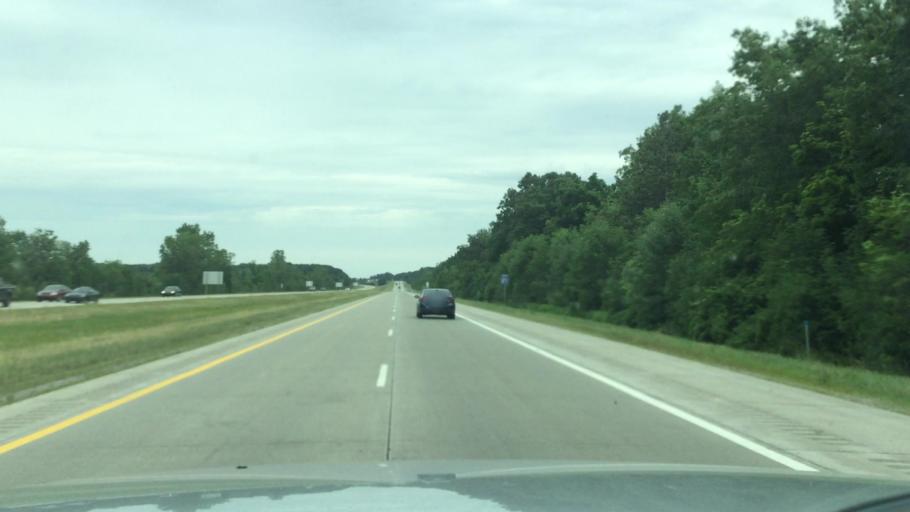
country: US
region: Michigan
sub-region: Genesee County
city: Grand Blanc
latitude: 42.9363
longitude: -83.6815
